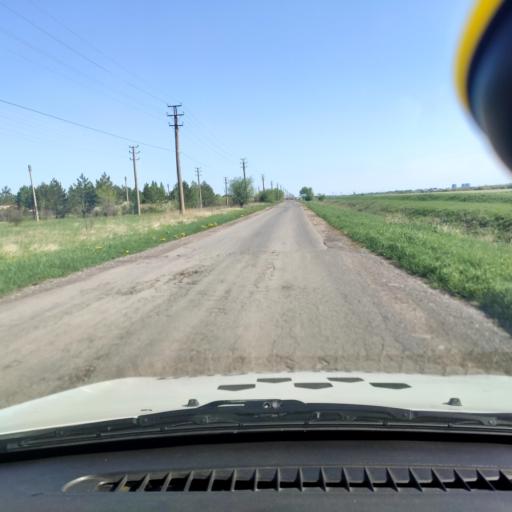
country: RU
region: Samara
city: Podstepki
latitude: 53.5329
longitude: 49.1987
